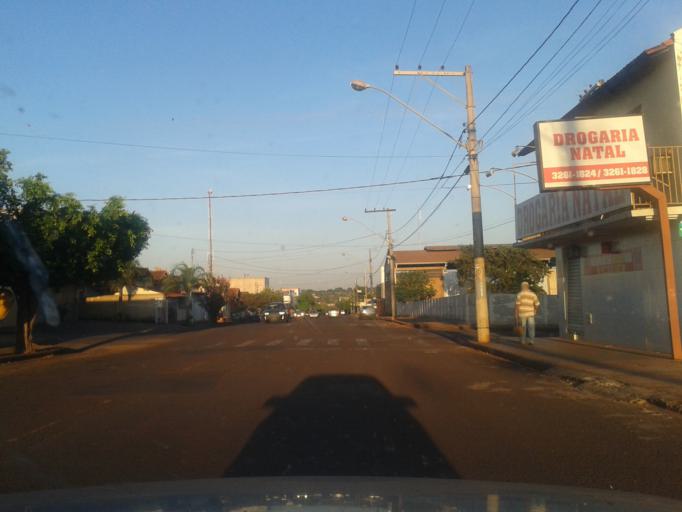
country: BR
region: Minas Gerais
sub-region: Ituiutaba
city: Ituiutaba
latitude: -18.9837
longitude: -49.4664
